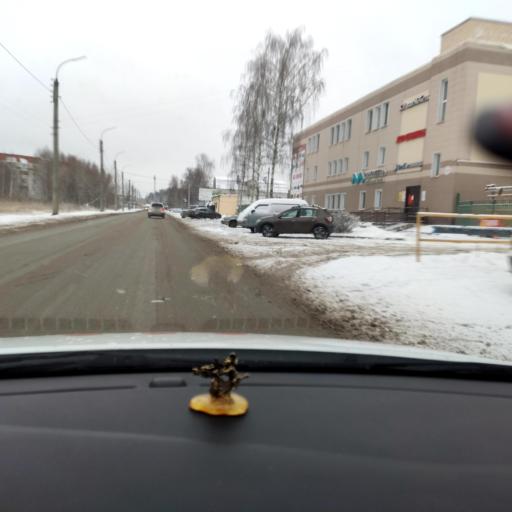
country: RU
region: Tatarstan
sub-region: Zelenodol'skiy Rayon
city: Zelenodolsk
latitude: 55.8651
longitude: 48.5474
